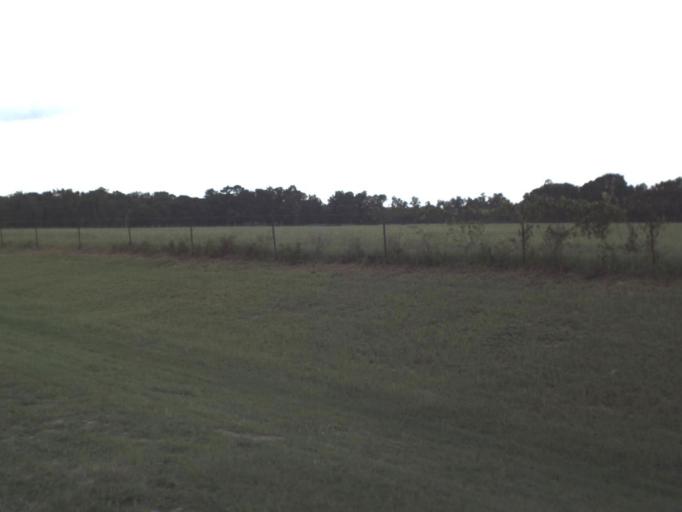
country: US
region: Florida
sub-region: Union County
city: Lake Butler
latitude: 29.8913
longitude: -82.3395
